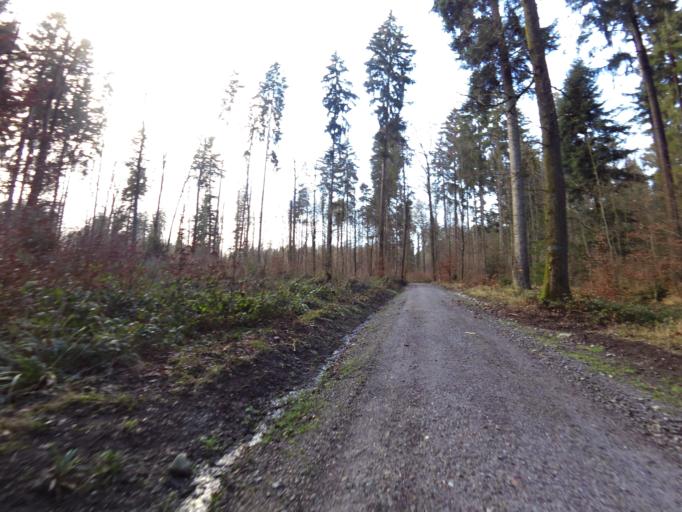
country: CH
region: Zurich
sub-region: Bezirk Dietikon
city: Uitikon
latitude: 47.3751
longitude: 8.4666
